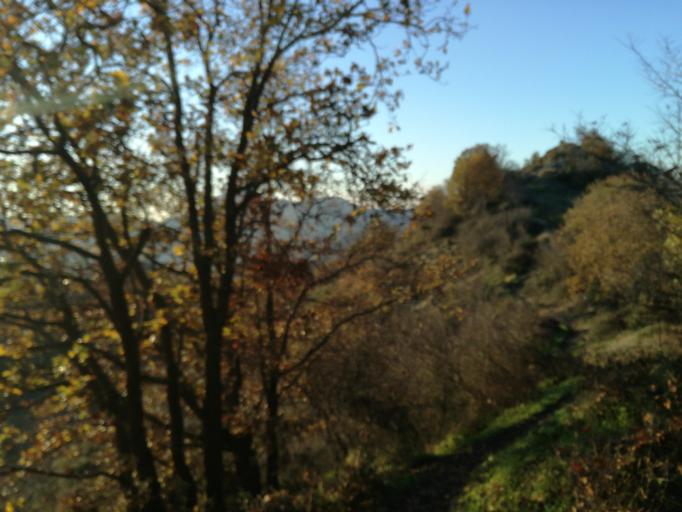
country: IT
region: Veneto
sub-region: Provincia di Padova
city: Montegrotto Terme
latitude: 45.3094
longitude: 11.7739
